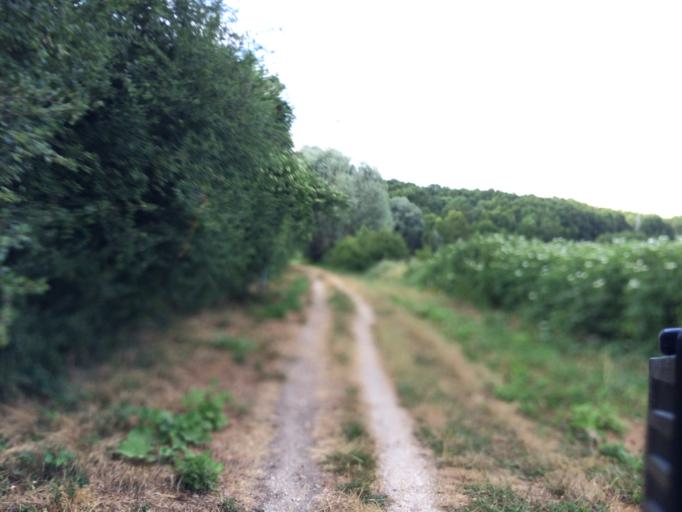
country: FR
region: Ile-de-France
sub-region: Departement de l'Essonne
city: Etiolles
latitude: 48.6389
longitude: 2.4918
